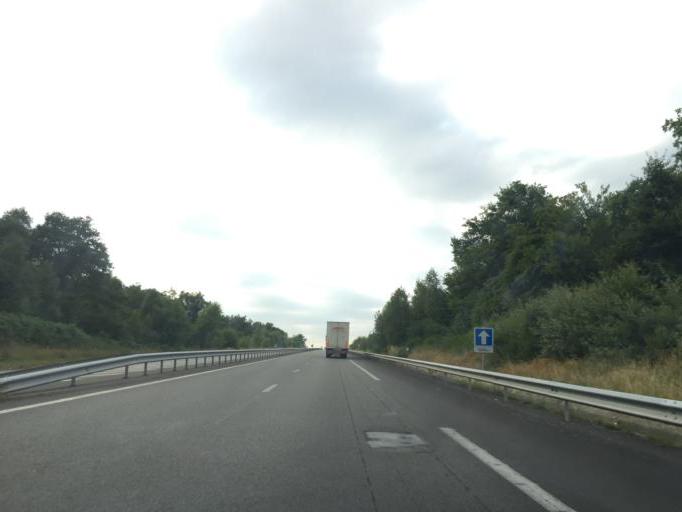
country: FR
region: Auvergne
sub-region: Departement de l'Allier
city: Diou
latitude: 46.5108
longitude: 3.7589
